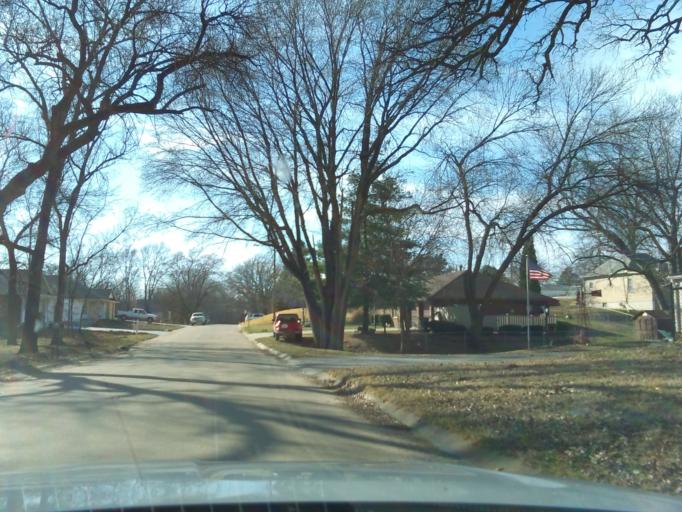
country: US
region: Nebraska
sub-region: Otoe County
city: Nebraska City
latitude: 40.6749
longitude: -95.8703
